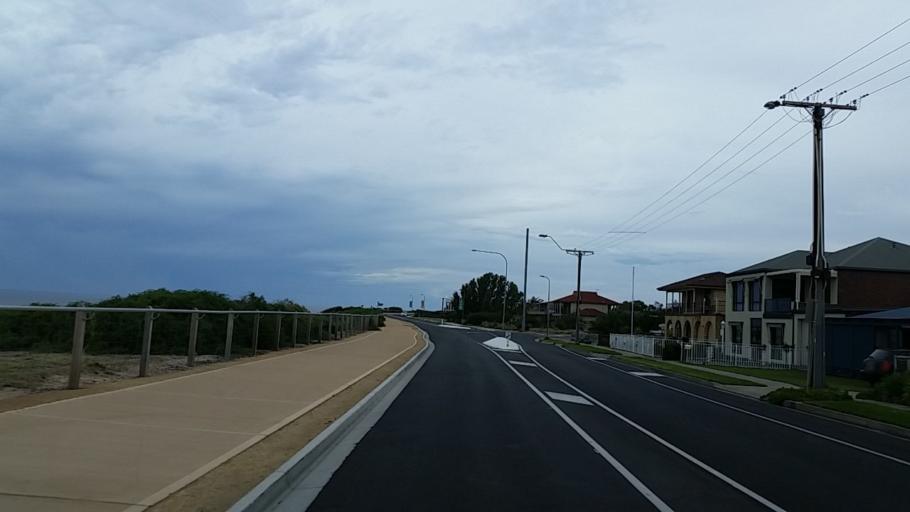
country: AU
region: South Australia
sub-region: Onkaparinga
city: Port Willunga
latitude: -35.2801
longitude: 138.4438
